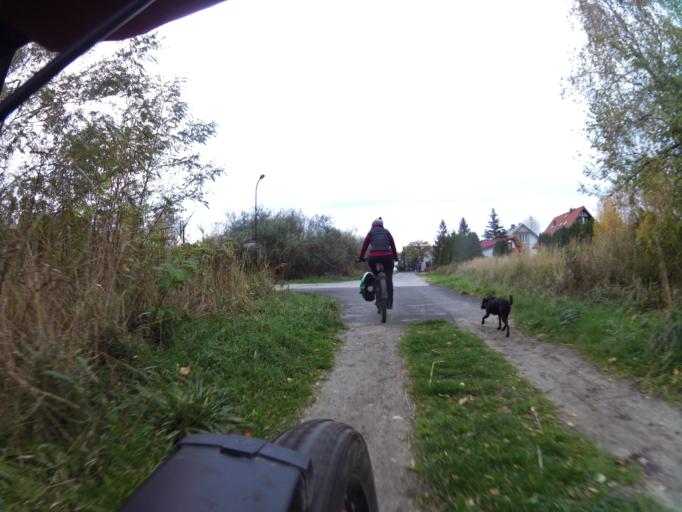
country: PL
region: Pomeranian Voivodeship
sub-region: Powiat pucki
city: Jastarnia
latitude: 54.7029
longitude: 18.6594
